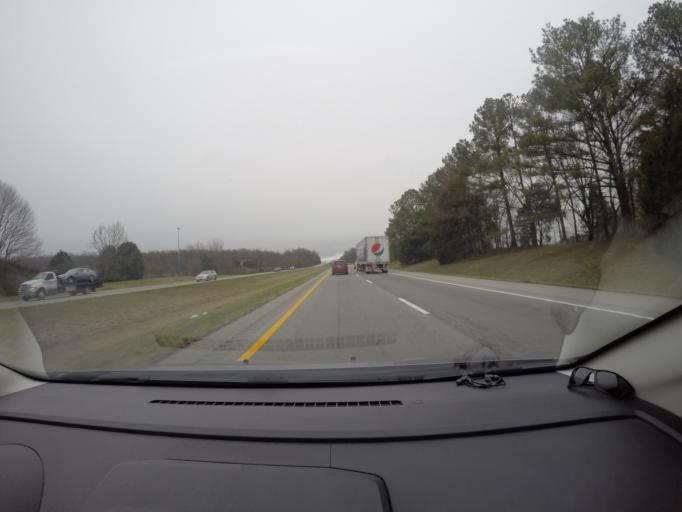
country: US
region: Tennessee
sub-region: Franklin County
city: Sewanee
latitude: 35.3416
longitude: -85.9414
